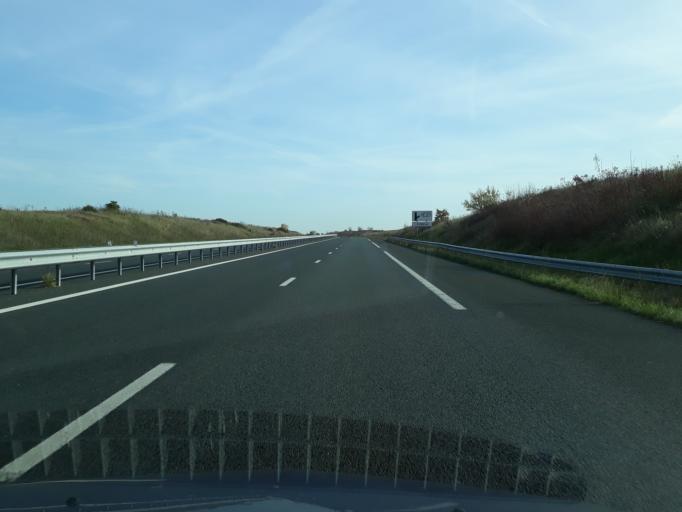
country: FR
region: Champagne-Ardenne
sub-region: Departement de l'Aube
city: Bucheres
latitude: 48.2229
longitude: 4.0982
